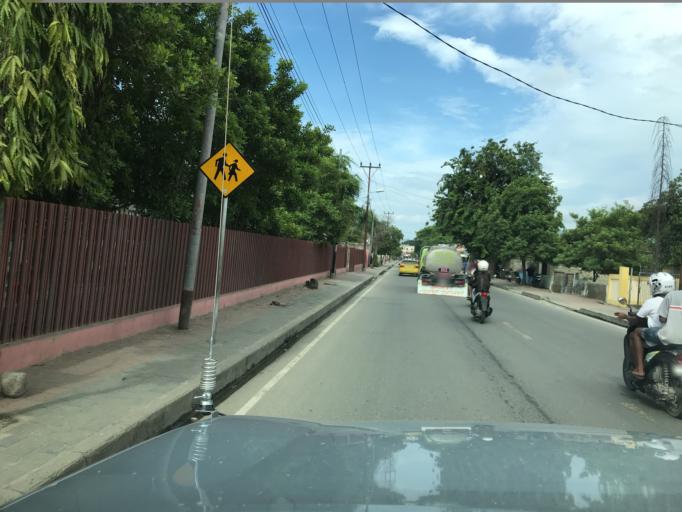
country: TL
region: Dili
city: Dili
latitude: -8.5582
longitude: 125.5664
